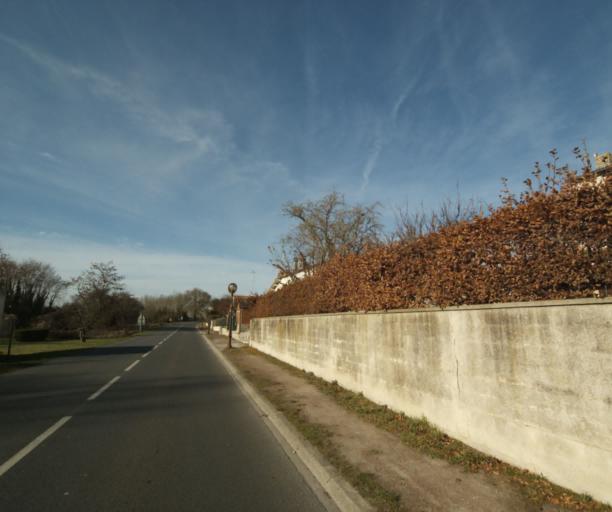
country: FR
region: Poitou-Charentes
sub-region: Departement de la Charente-Maritime
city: Chaniers
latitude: 45.7201
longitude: -0.5636
